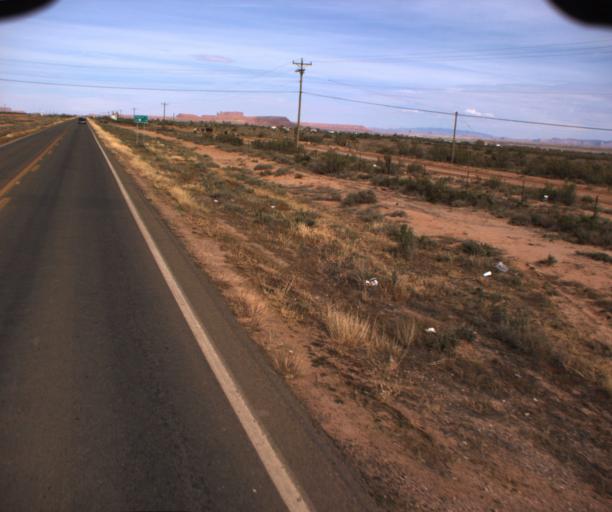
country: US
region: Arizona
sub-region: Apache County
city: Many Farms
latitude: 36.3666
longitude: -109.6136
